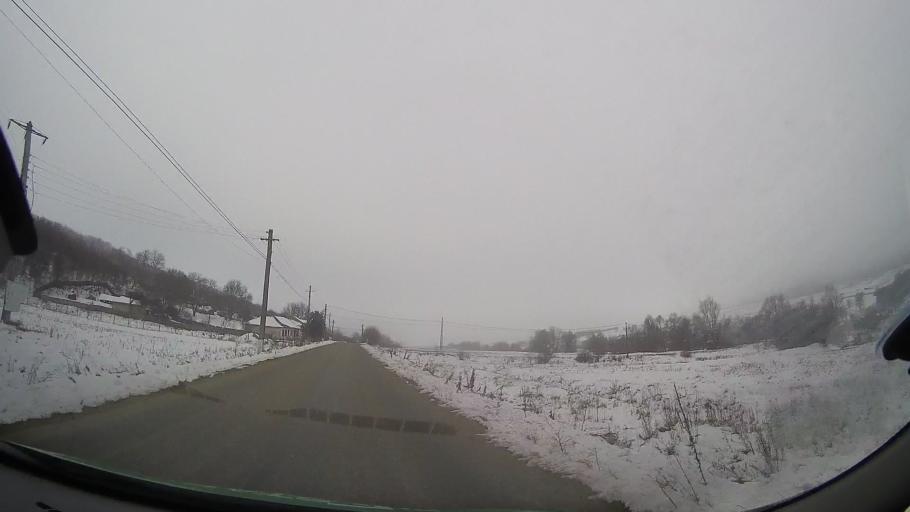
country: RO
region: Bacau
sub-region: Comuna Vultureni
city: Vultureni
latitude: 46.3276
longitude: 27.2915
